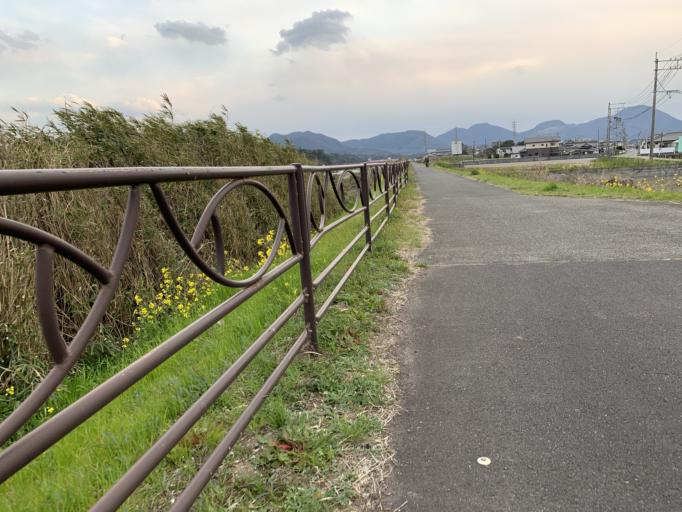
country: JP
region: Oita
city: Bungo-Takada-shi
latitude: 33.5409
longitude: 131.3541
